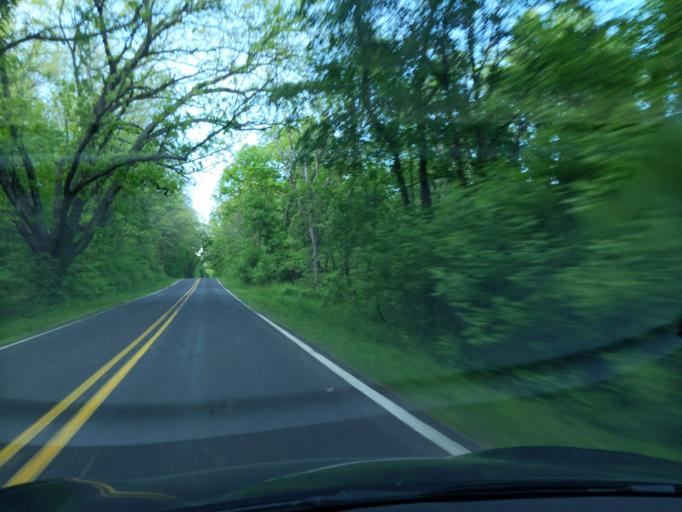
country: US
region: Michigan
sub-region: Ingham County
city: Stockbridge
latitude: 42.5170
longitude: -84.3056
